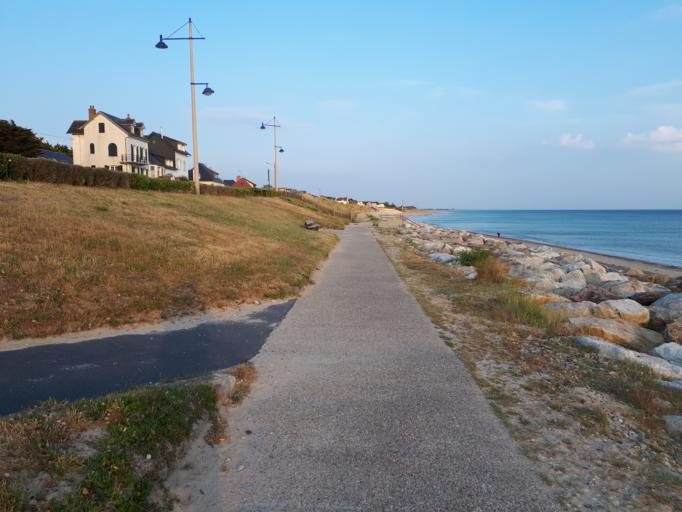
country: FR
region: Lower Normandy
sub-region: Departement de la Manche
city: Barneville-Plage
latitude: 49.3656
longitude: -1.7685
